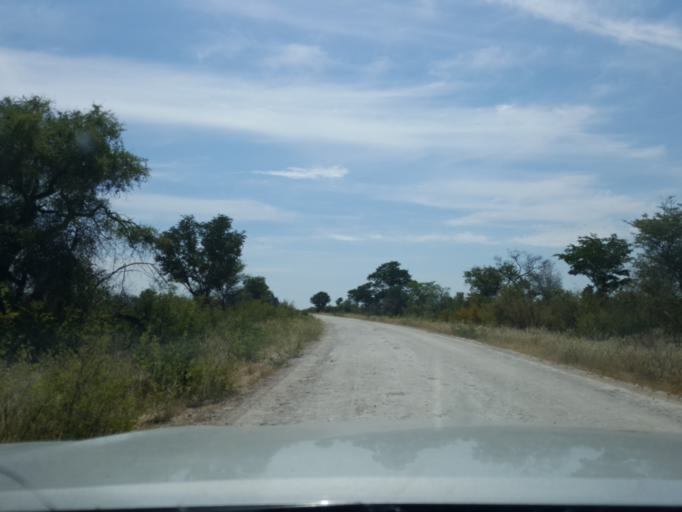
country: BW
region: North West
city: Shakawe
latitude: -18.7693
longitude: 21.7861
